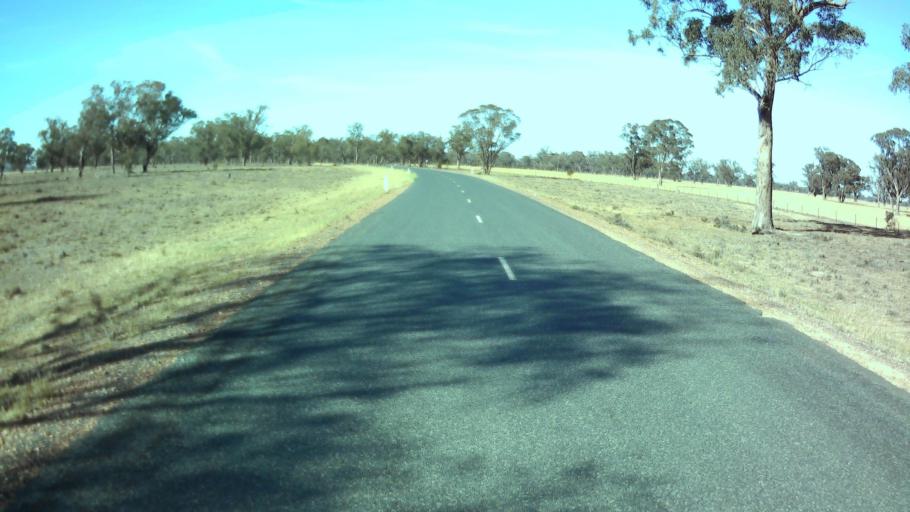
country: AU
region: New South Wales
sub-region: Weddin
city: Grenfell
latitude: -34.0580
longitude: 147.9124
